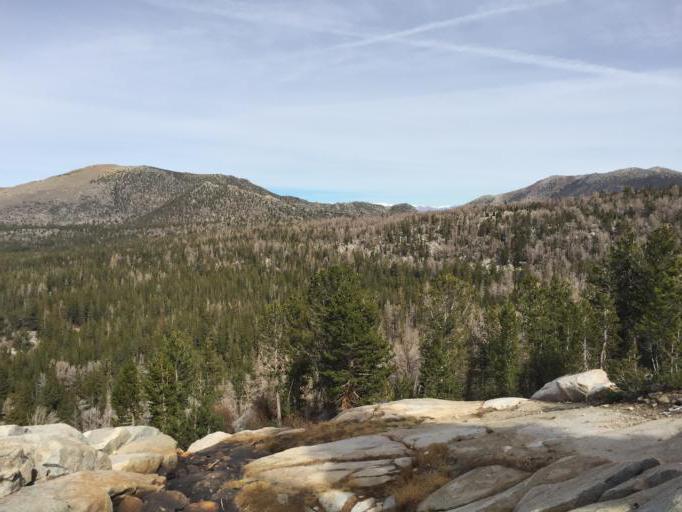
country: US
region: California
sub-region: Mono County
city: Mammoth Lakes
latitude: 37.4853
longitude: -118.7550
